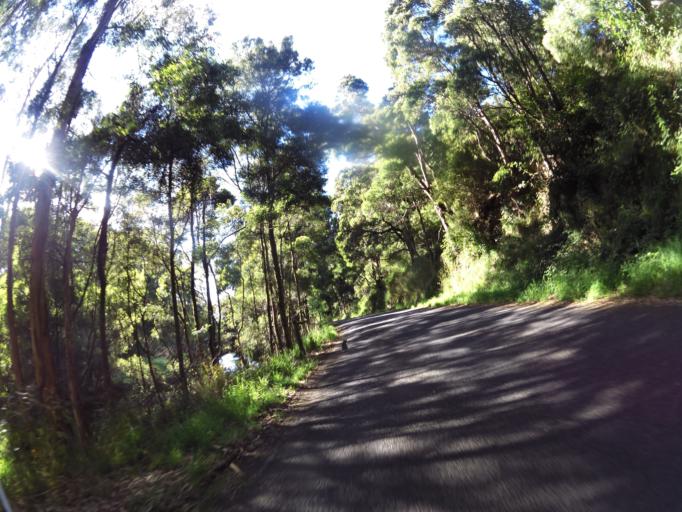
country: AU
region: Victoria
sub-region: Colac-Otway
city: Apollo Bay
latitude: -38.7628
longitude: 143.6304
